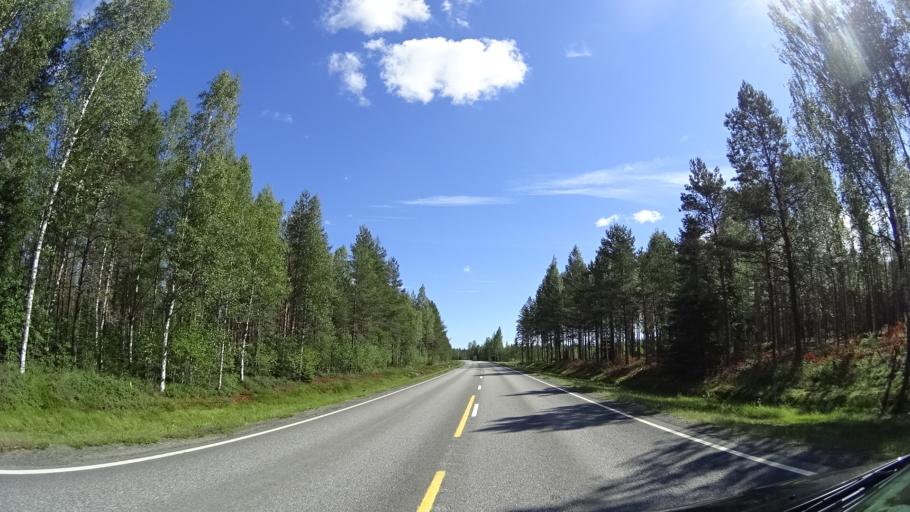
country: FI
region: Pirkanmaa
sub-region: Luoteis-Pirkanmaa
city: Kihnioe
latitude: 62.2195
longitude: 23.2713
